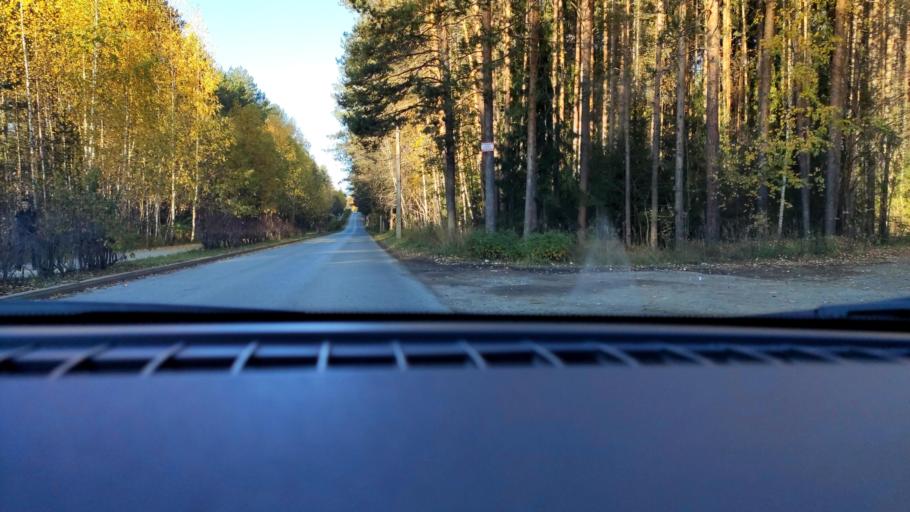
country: RU
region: Perm
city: Perm
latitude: 58.0551
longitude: 56.2263
